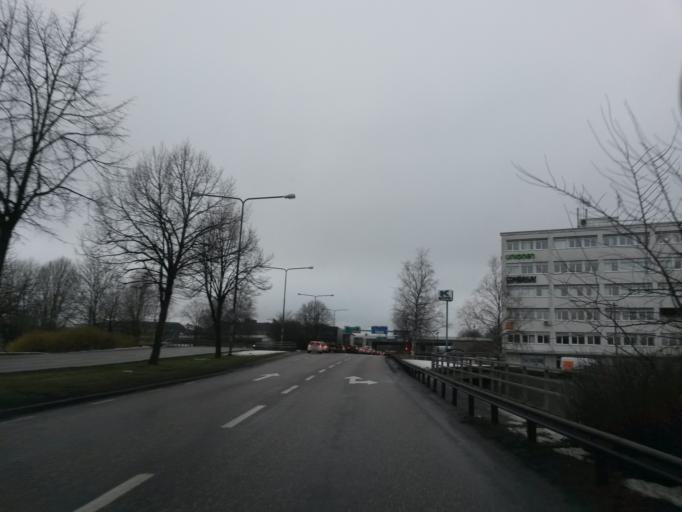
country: SE
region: Vaestra Goetaland
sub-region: Boras Kommun
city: Boras
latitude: 57.7139
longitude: 12.9464
